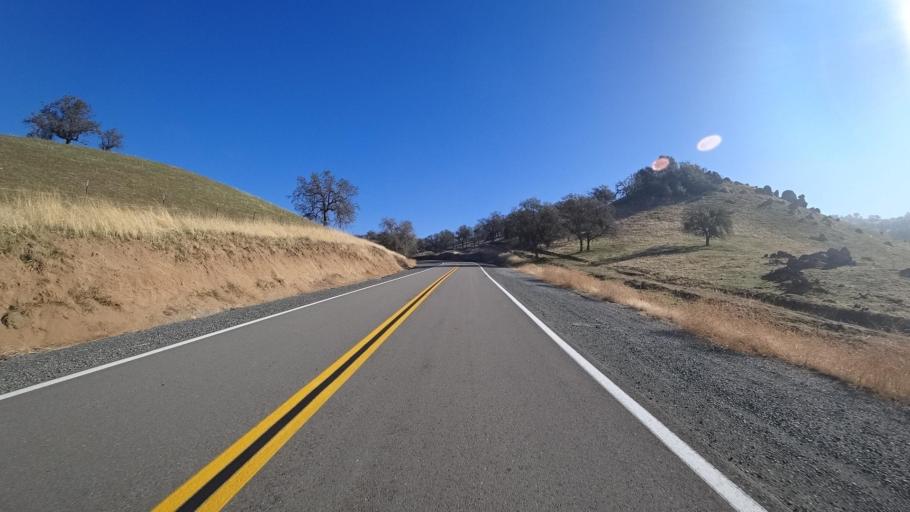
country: US
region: California
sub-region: Kern County
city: Alta Sierra
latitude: 35.7194
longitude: -118.8037
